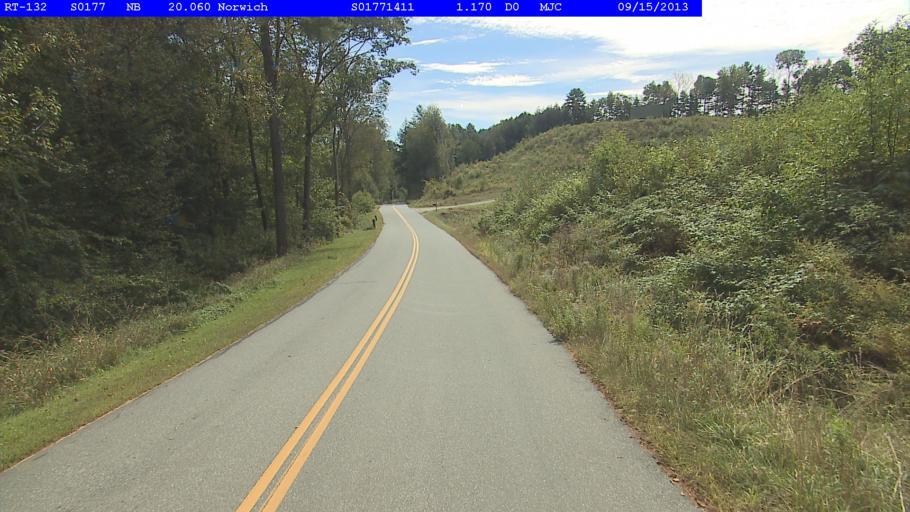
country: US
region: New Hampshire
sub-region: Grafton County
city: Hanover
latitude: 43.7715
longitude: -72.2534
